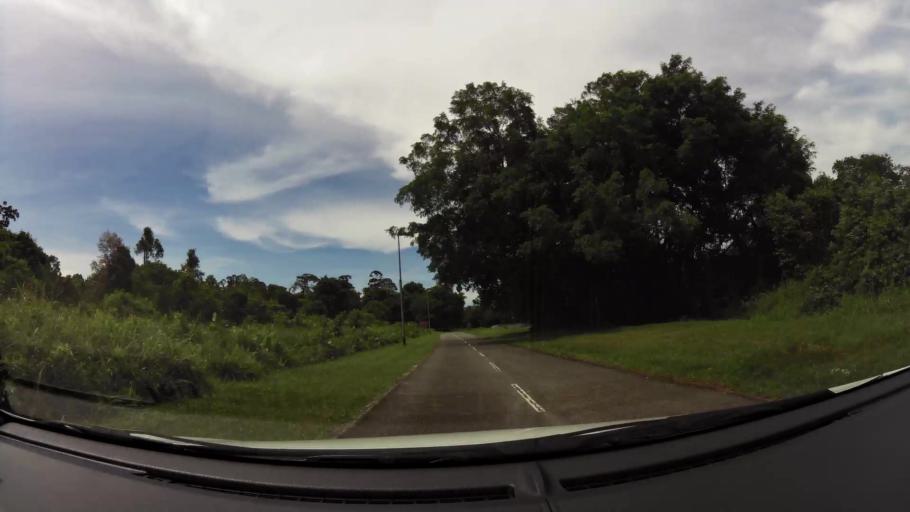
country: BN
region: Belait
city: Seria
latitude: 4.5938
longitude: 114.2839
